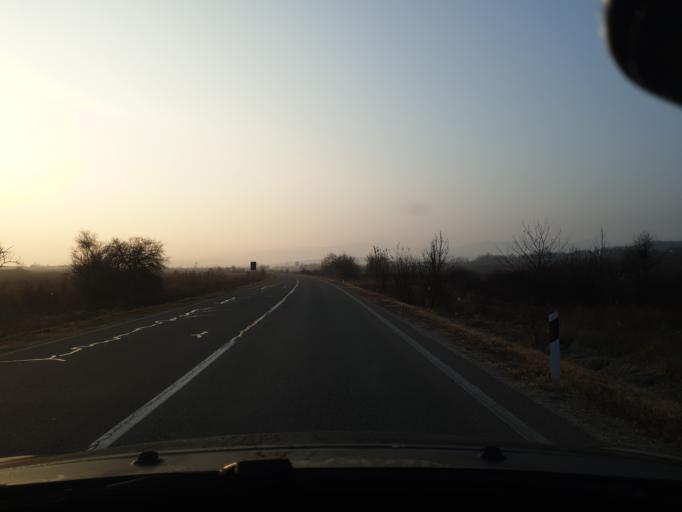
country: RS
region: Central Serbia
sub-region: Jablanicki Okrug
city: Leskovac
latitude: 42.9461
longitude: 21.9923
